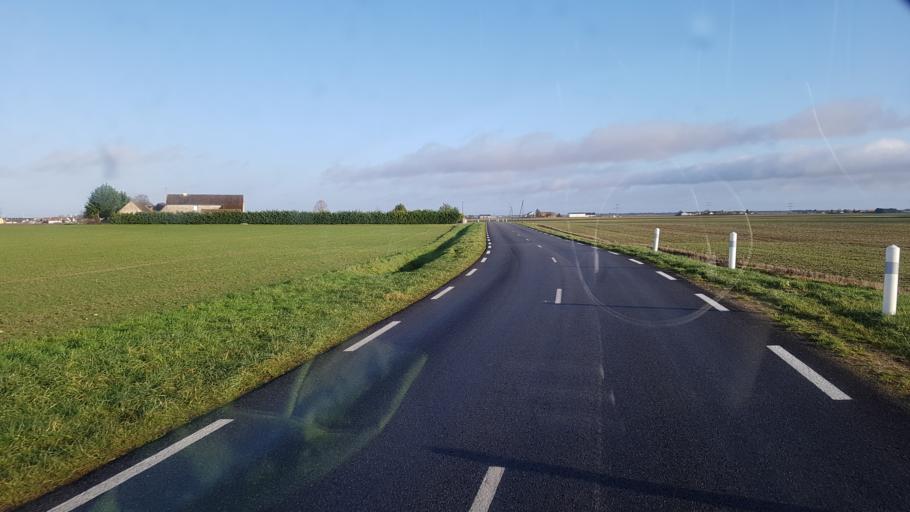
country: FR
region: Centre
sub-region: Departement du Loiret
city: Dadonville
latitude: 48.0910
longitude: 2.2370
